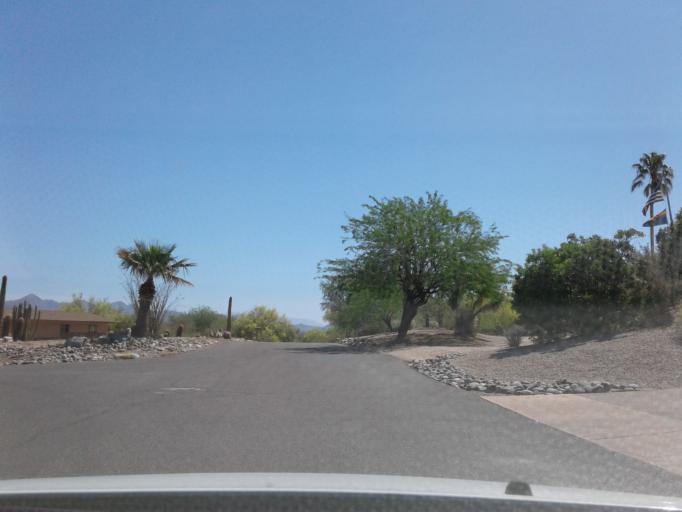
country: US
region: Arizona
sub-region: Maricopa County
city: Paradise Valley
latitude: 33.5597
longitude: -111.9825
